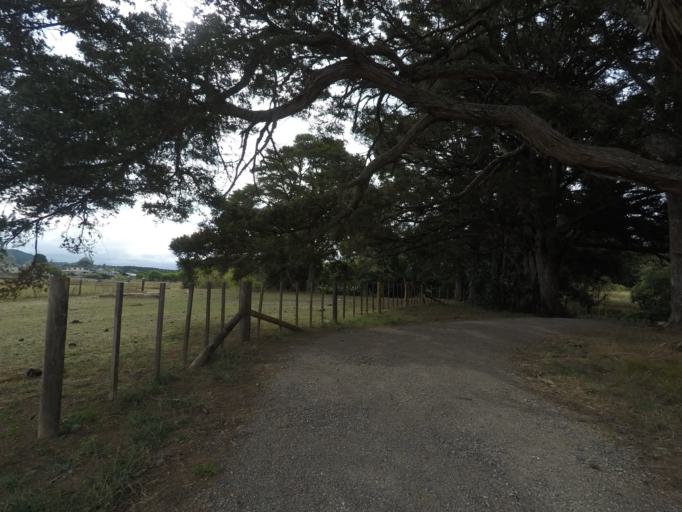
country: NZ
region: Northland
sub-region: Whangarei
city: Whangarei
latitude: -35.6762
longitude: 174.3324
